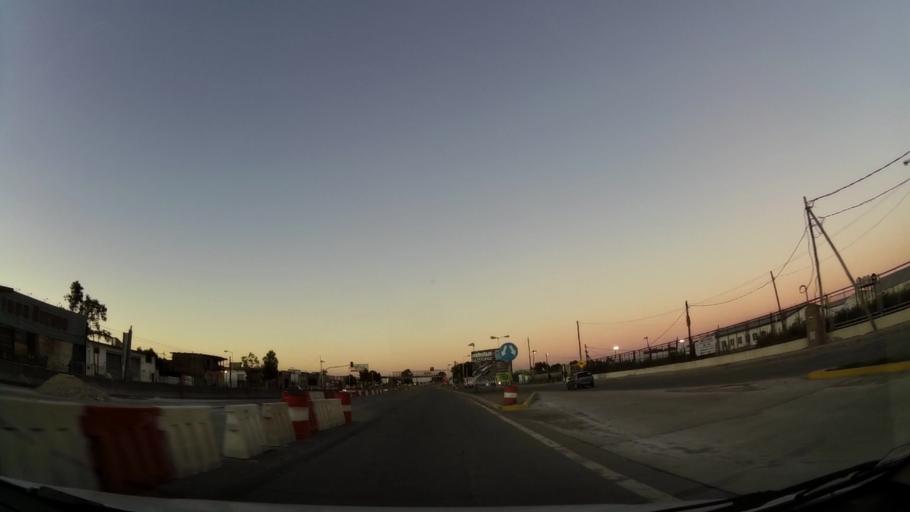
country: AR
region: Buenos Aires
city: San Justo
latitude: -34.7294
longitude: -58.6009
